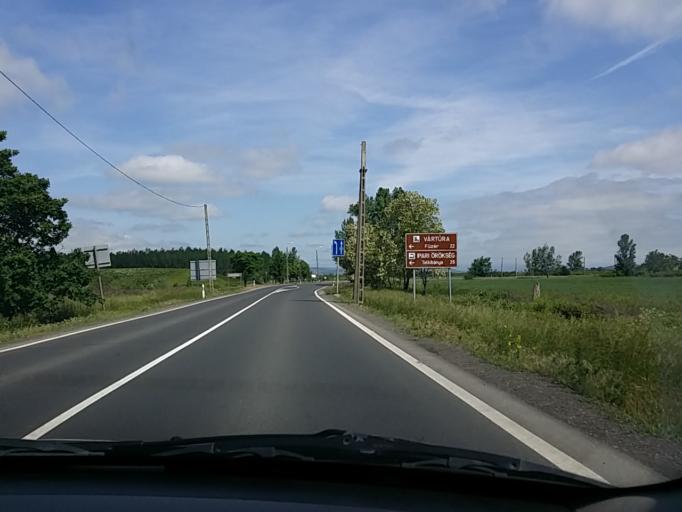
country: HU
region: Borsod-Abauj-Zemplen
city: Satoraljaujhely
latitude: 48.4171
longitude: 21.6441
